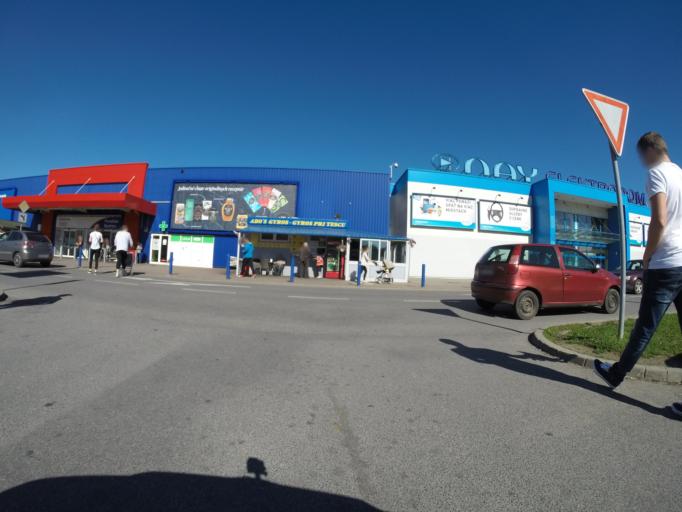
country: SK
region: Trenciansky
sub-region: Okres Povazska Bystrica
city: Povazska Bystrica
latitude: 49.1028
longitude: 18.4611
